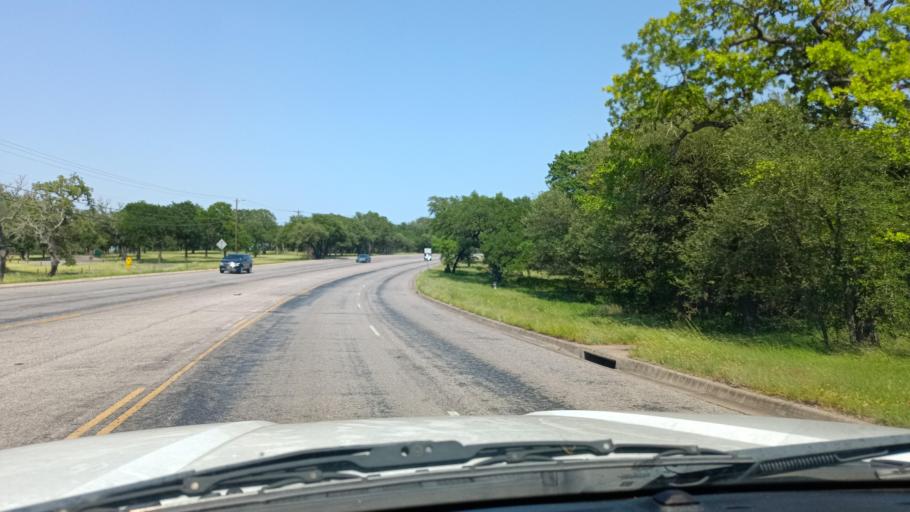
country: US
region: Texas
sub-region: Bell County
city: Morgans Point Resort
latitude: 31.1035
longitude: -97.4824
